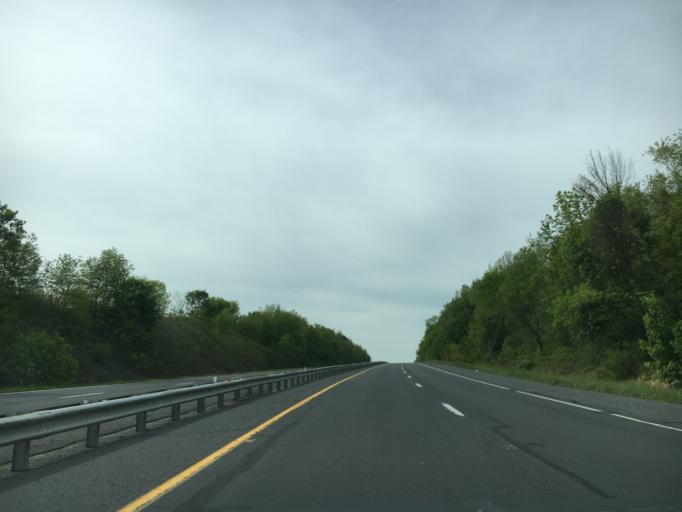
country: US
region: Pennsylvania
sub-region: Lehigh County
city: Cementon
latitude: 40.7049
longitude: -75.5208
